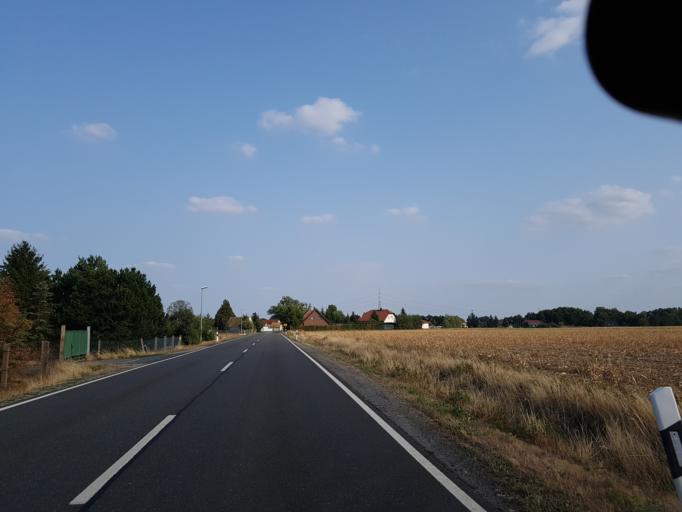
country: DE
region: Saxony-Anhalt
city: Pretzsch
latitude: 51.6717
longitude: 12.8357
